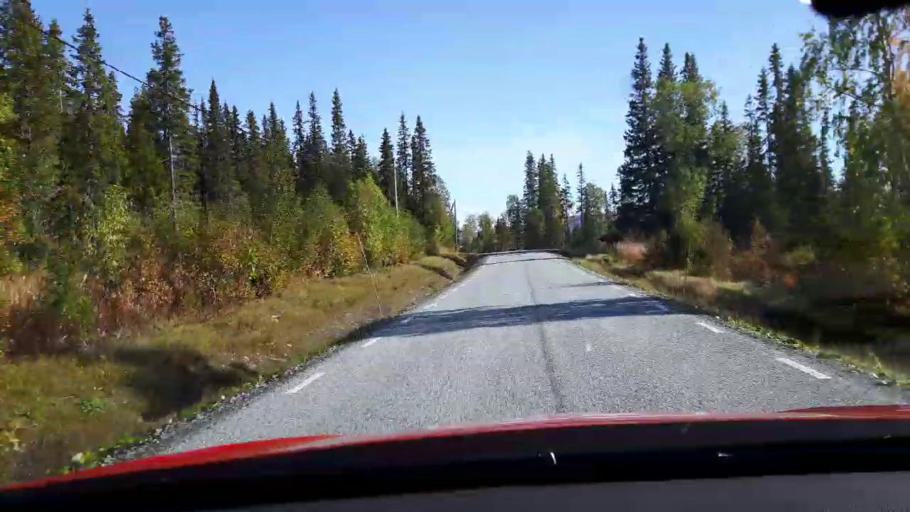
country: NO
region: Nord-Trondelag
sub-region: Royrvik
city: Royrvik
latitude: 64.8134
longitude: 14.1557
